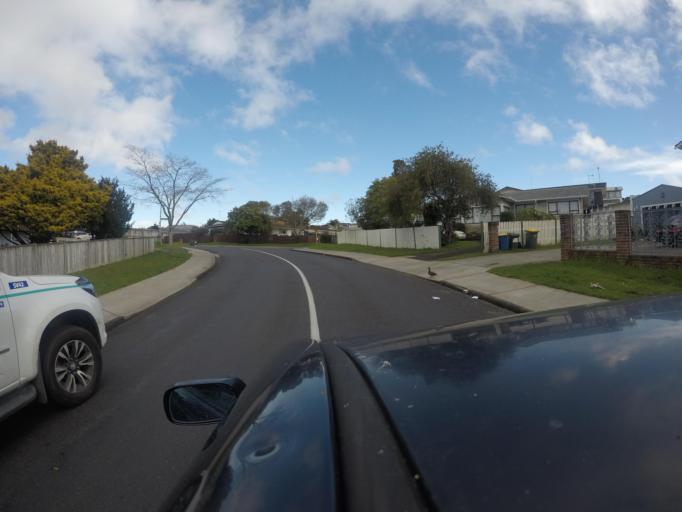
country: NZ
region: Auckland
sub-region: Auckland
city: Waitakere
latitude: -36.8954
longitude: 174.6496
